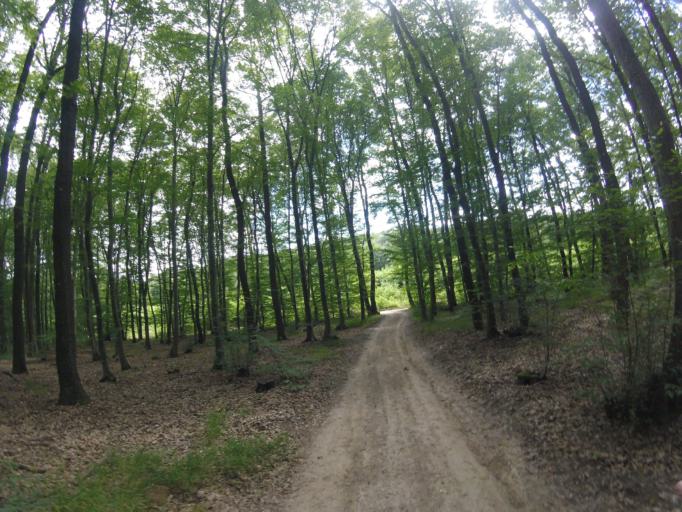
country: HU
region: Nograd
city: Romhany
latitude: 47.8847
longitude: 19.2460
